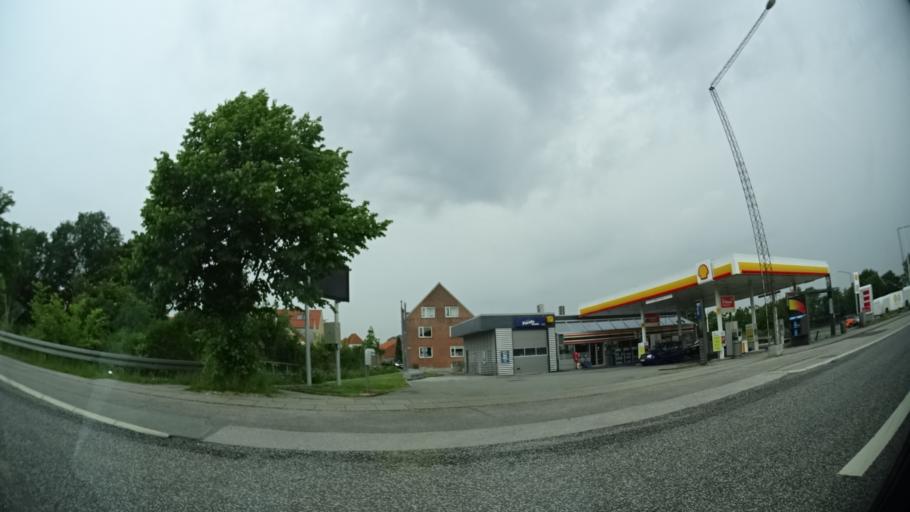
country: DK
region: Central Jutland
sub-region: Arhus Kommune
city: Arhus
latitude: 56.1952
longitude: 10.2198
